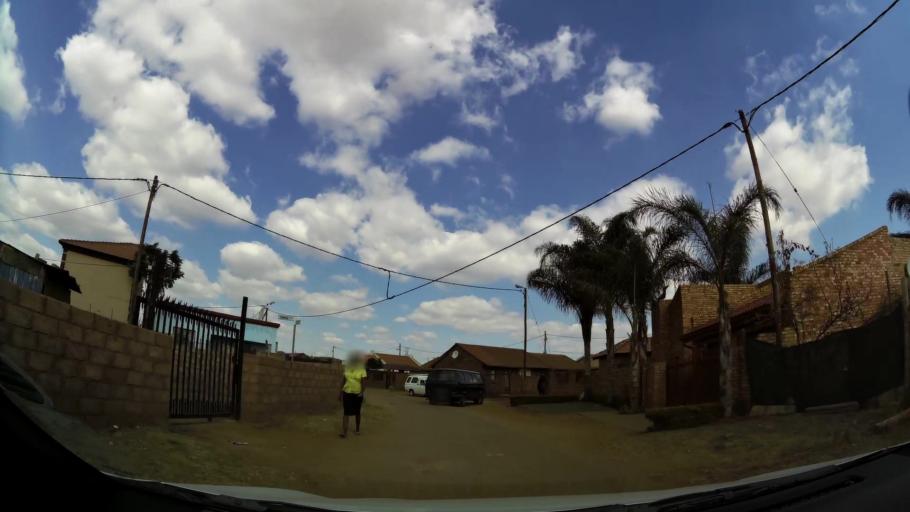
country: ZA
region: Gauteng
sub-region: City of Tshwane Metropolitan Municipality
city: Cullinan
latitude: -25.7126
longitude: 28.3990
